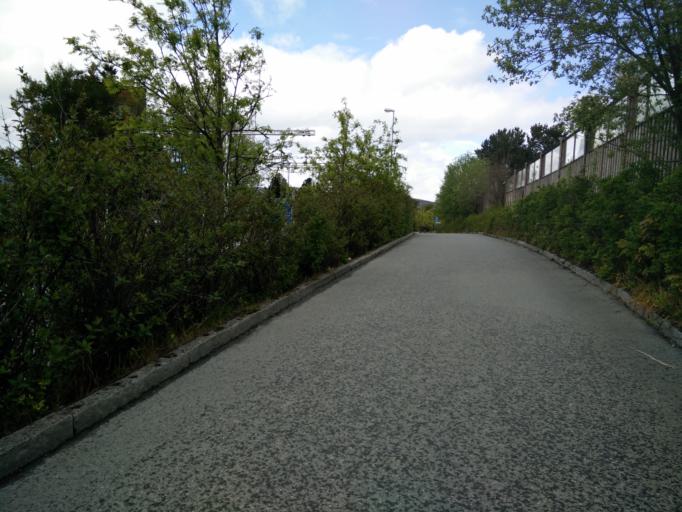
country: NO
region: Sor-Trondelag
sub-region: Trondheim
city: Trondheim
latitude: 63.4021
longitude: 10.4014
